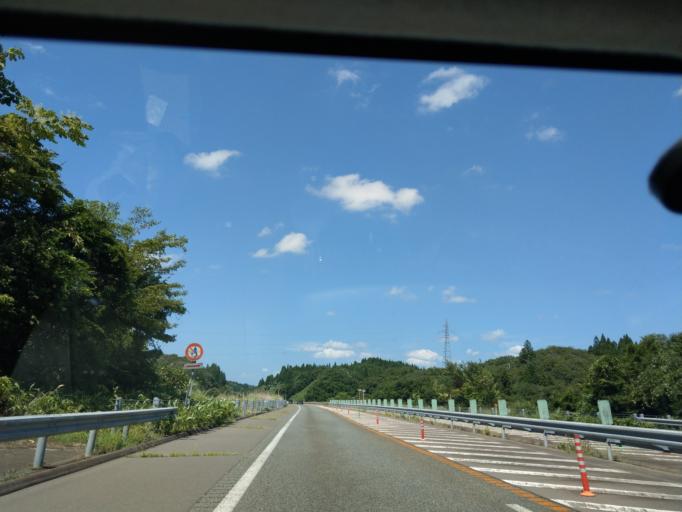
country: JP
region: Akita
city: Akita
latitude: 39.6679
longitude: 140.1884
